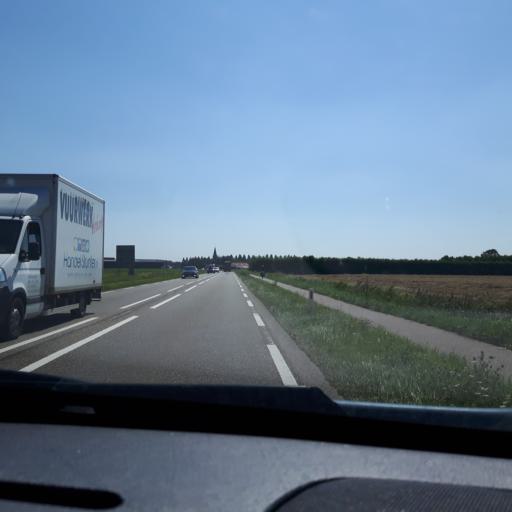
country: NL
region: Zeeland
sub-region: Gemeente Reimerswaal
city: Yerseke
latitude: 51.4581
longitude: 4.0279
